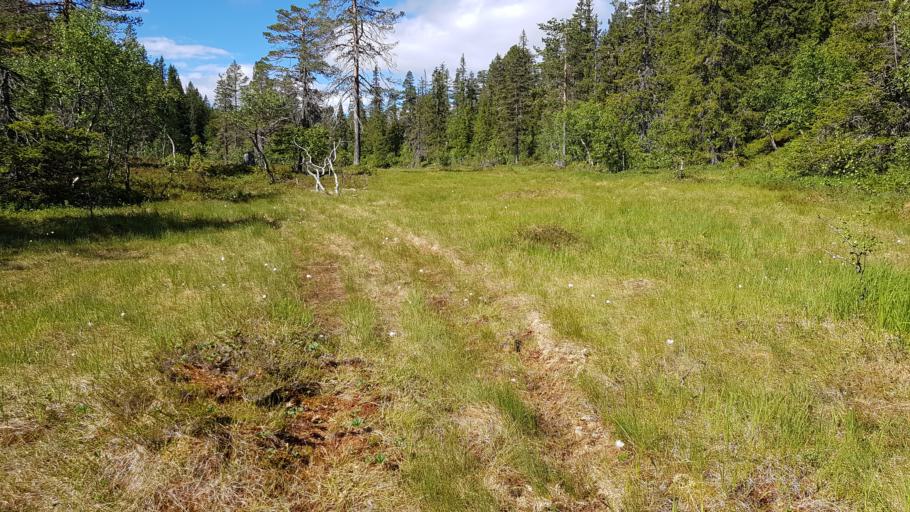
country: NO
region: Buskerud
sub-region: Rollag
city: Rollag
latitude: 60.1684
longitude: 9.3018
